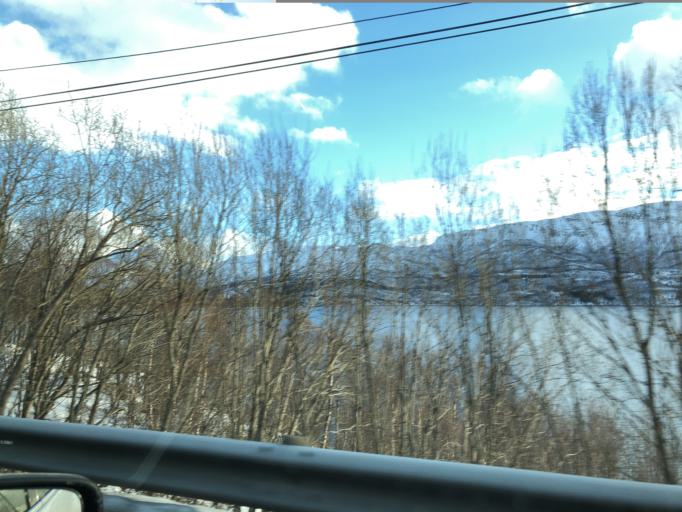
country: NO
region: Nordland
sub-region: Narvik
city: Bjerkvik
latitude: 68.4642
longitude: 17.6730
